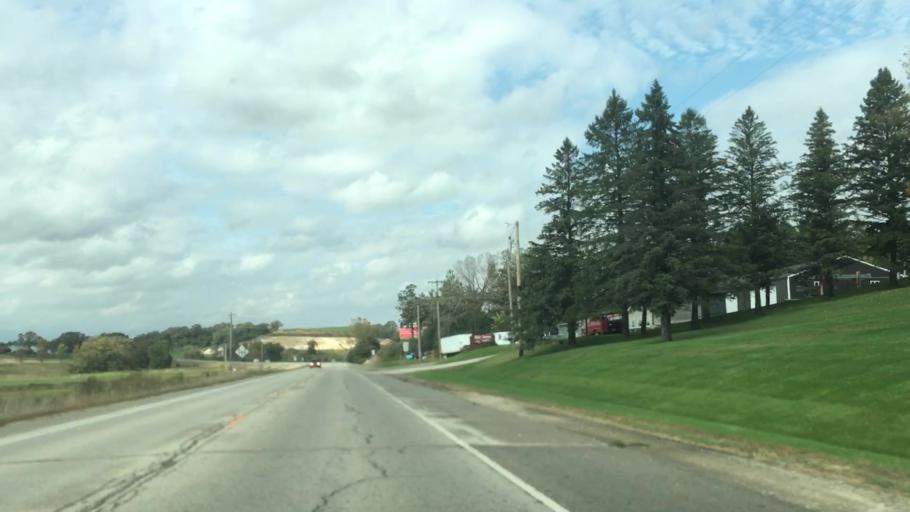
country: US
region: Minnesota
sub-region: Fillmore County
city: Chatfield
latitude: 43.8598
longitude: -92.1953
